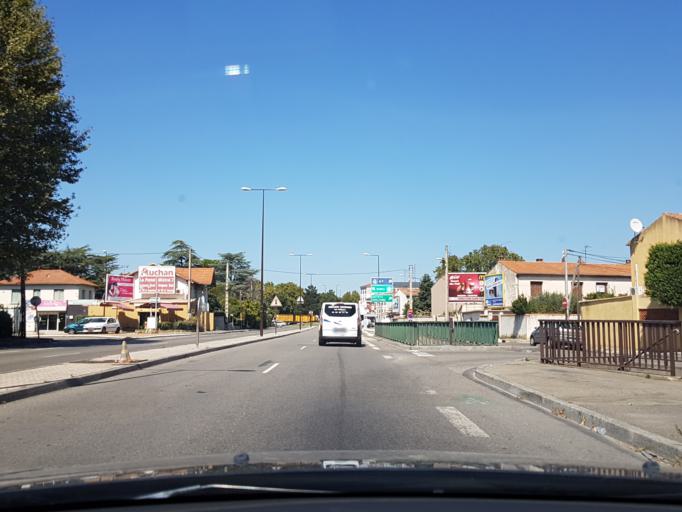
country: FR
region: Provence-Alpes-Cote d'Azur
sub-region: Departement du Vaucluse
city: Avignon
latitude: 43.9265
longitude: 4.8095
